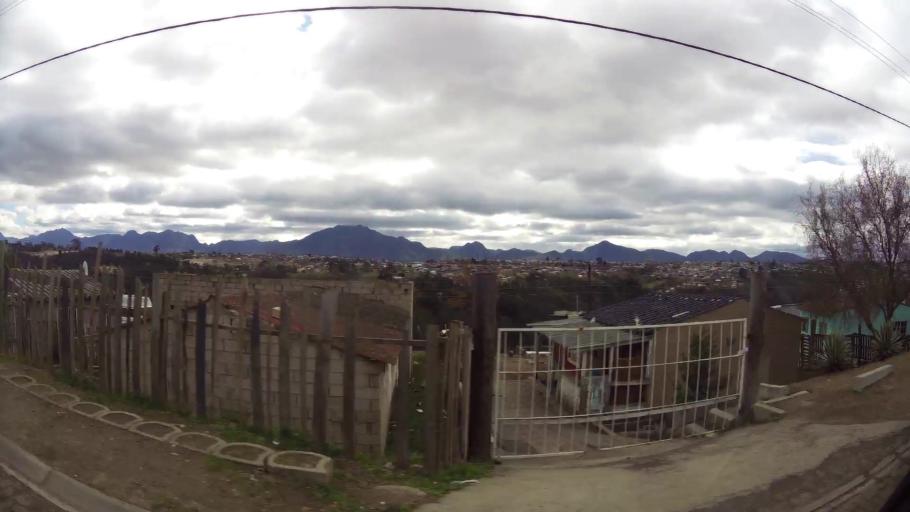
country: ZA
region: Western Cape
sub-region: Eden District Municipality
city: George
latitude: -34.0136
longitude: 22.4796
